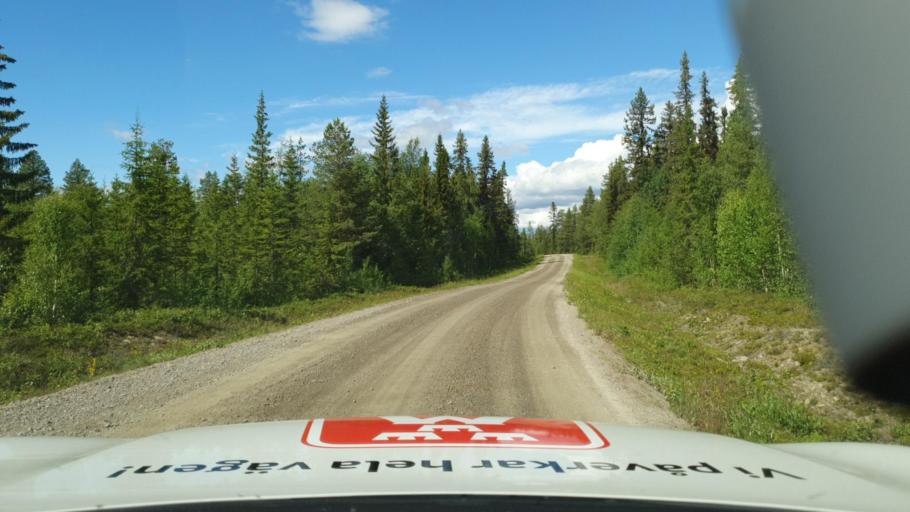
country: SE
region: Vaesterbotten
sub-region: Sorsele Kommun
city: Sorsele
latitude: 65.6705
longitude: 17.2174
